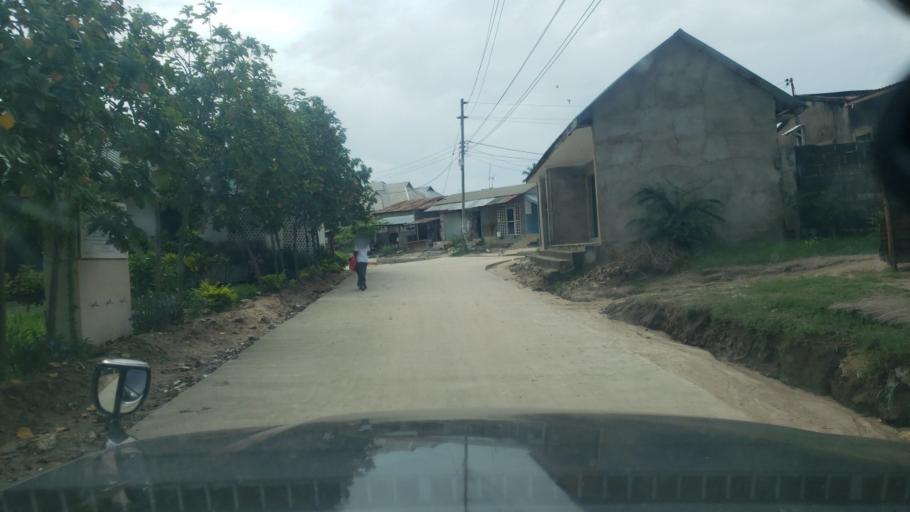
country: TZ
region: Pwani
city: Vikindu
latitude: -6.9232
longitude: 39.2552
